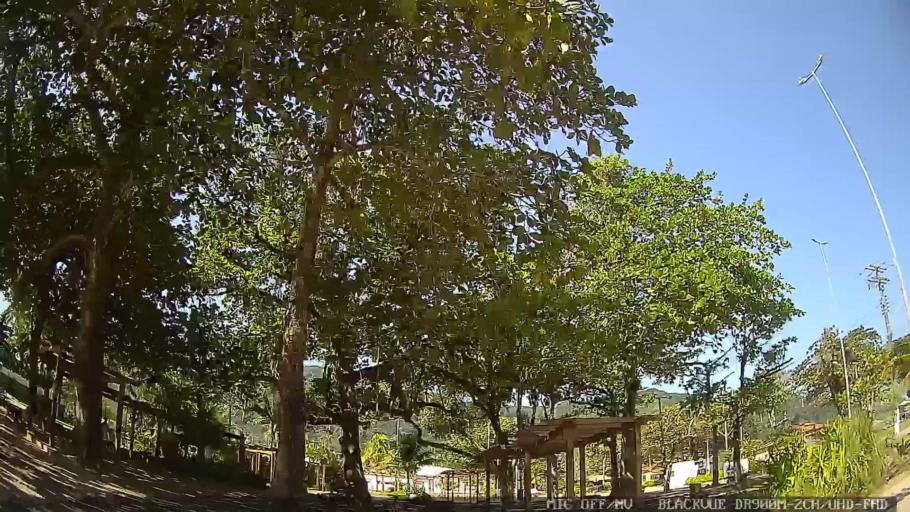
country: BR
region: Sao Paulo
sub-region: Guaruja
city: Guaruja
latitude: -24.0192
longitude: -46.2971
